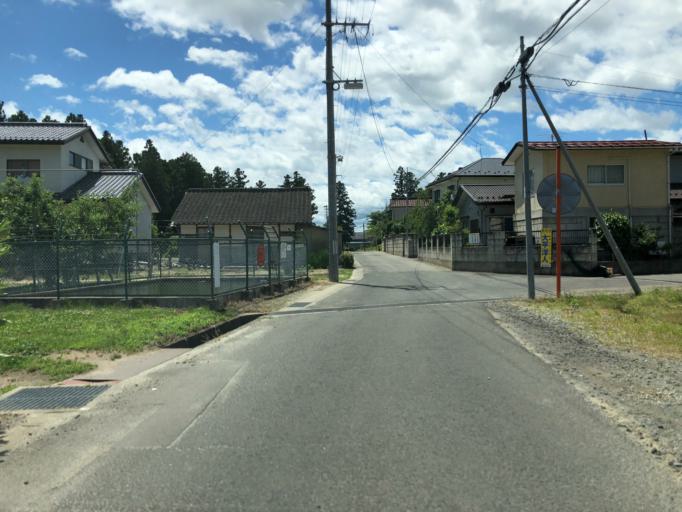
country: JP
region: Fukushima
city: Fukushima-shi
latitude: 37.8003
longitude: 140.4007
